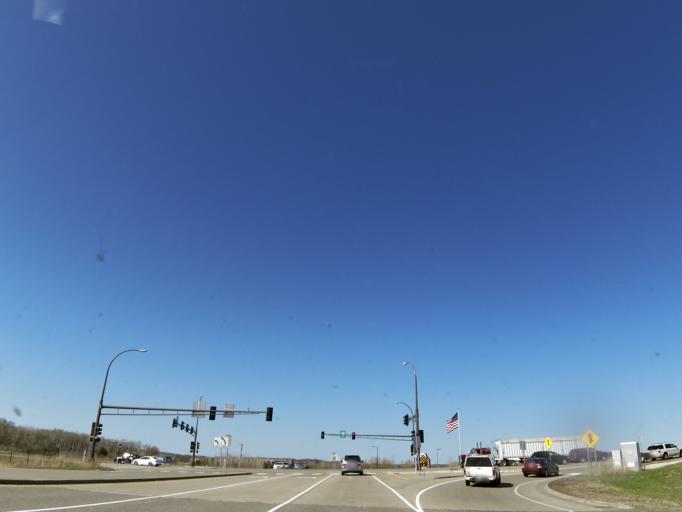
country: US
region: Minnesota
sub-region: Dakota County
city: Lakeville
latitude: 44.6445
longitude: -93.2990
